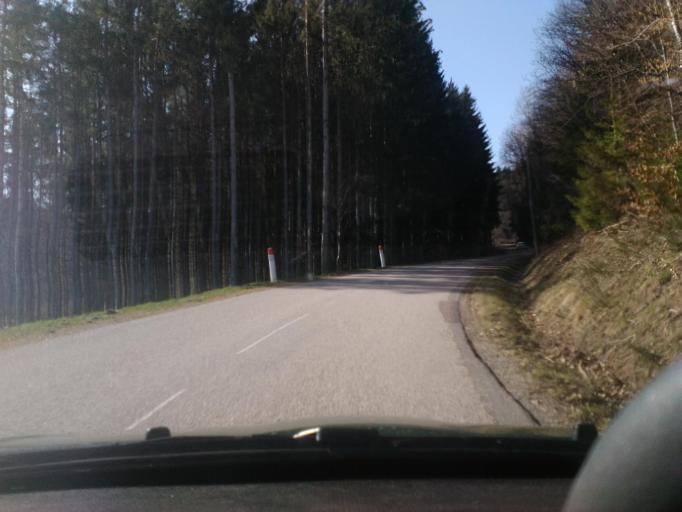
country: FR
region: Lorraine
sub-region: Departement des Vosges
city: Ban-de-Laveline
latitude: 48.3392
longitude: 7.0624
